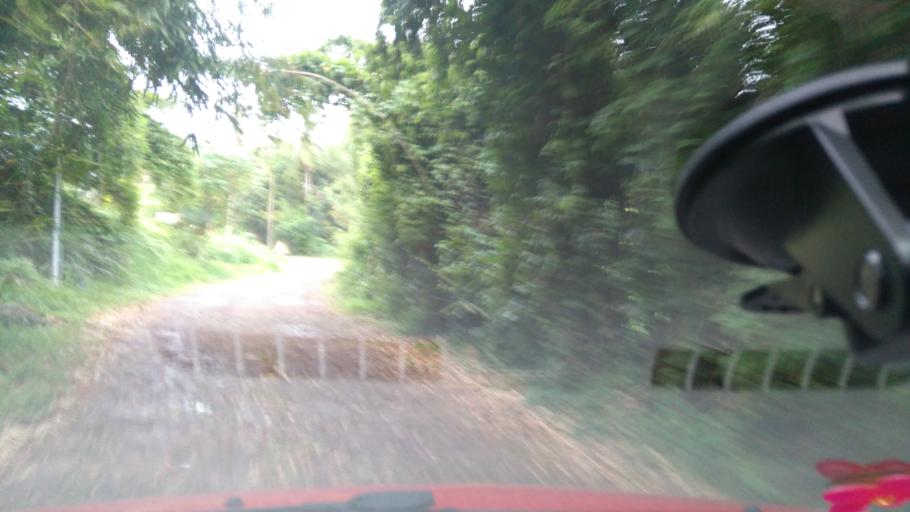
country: MQ
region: Martinique
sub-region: Martinique
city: Ducos
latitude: 14.5532
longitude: -60.9680
